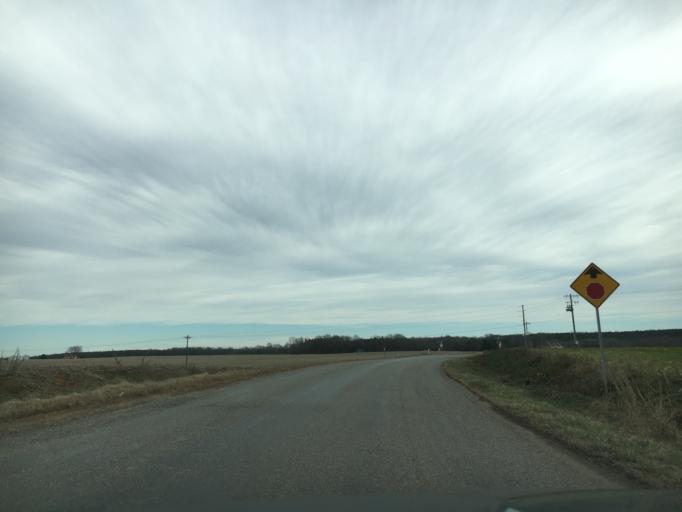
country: US
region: Virginia
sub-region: Amelia County
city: Amelia Court House
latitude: 37.4034
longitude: -77.9694
